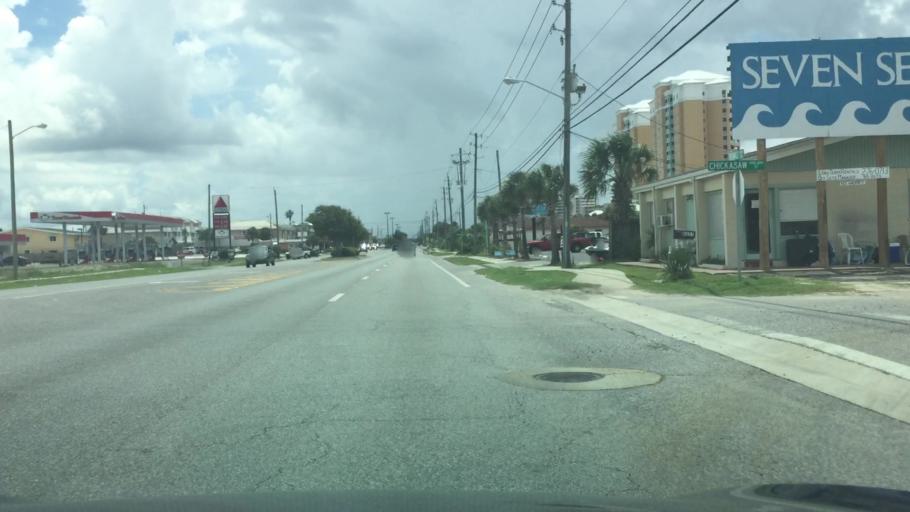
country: US
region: Florida
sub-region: Bay County
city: Panama City Beach
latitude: 30.1625
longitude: -85.7814
